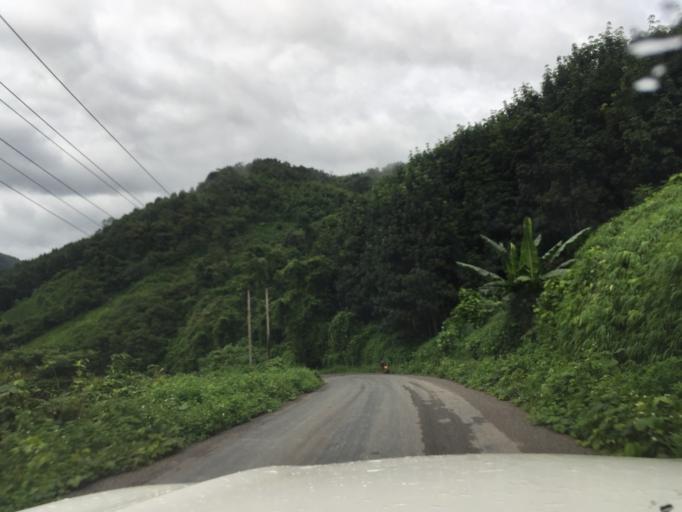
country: LA
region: Oudomxai
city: Muang La
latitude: 21.0166
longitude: 102.2319
